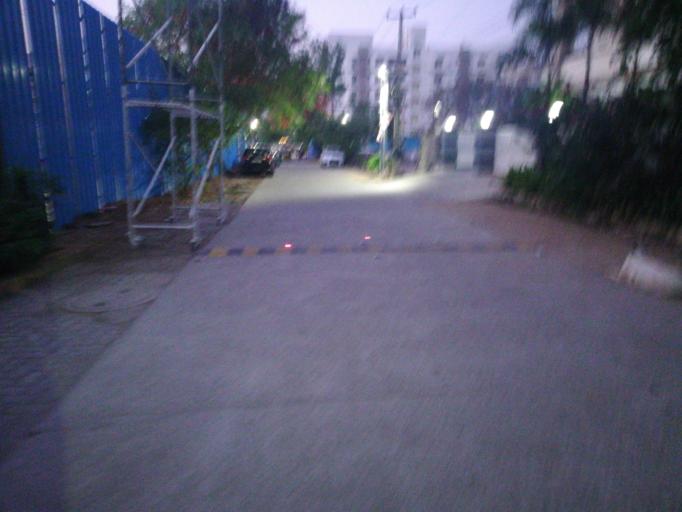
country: IN
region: Telangana
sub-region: Rangareddi
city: Kukatpalli
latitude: 17.4608
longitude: 78.3682
